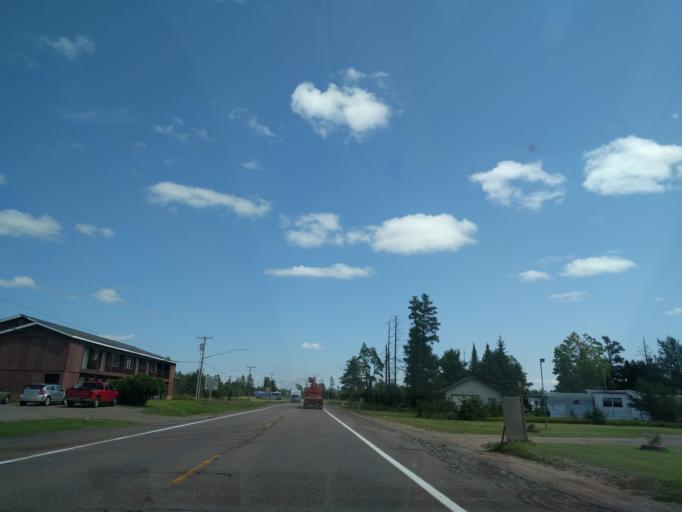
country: US
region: Michigan
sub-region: Marquette County
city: Gwinn
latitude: 46.2759
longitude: -87.4129
